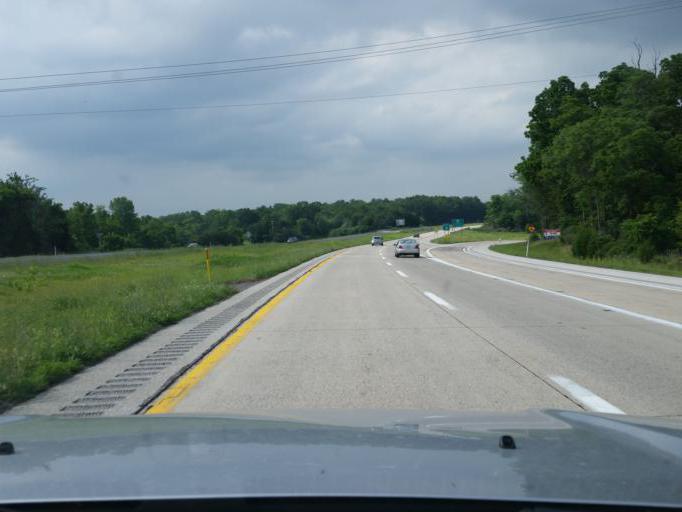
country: US
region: Pennsylvania
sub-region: Adams County
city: Lake Heritage
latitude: 39.8215
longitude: -77.1980
